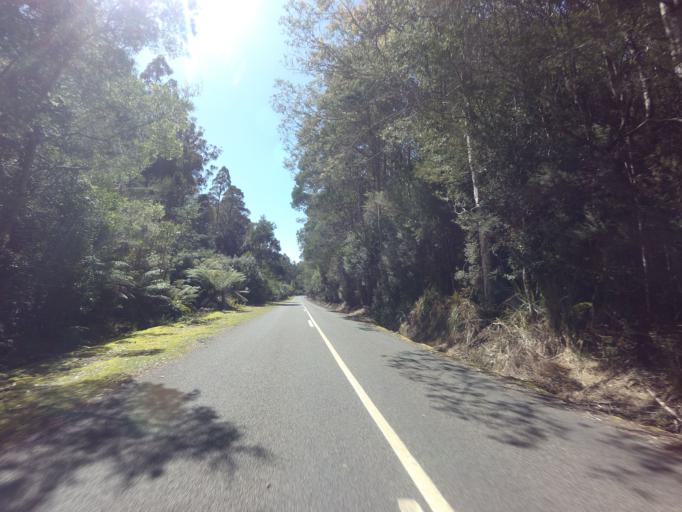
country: AU
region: Tasmania
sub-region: Derwent Valley
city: New Norfolk
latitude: -42.7523
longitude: 146.5153
